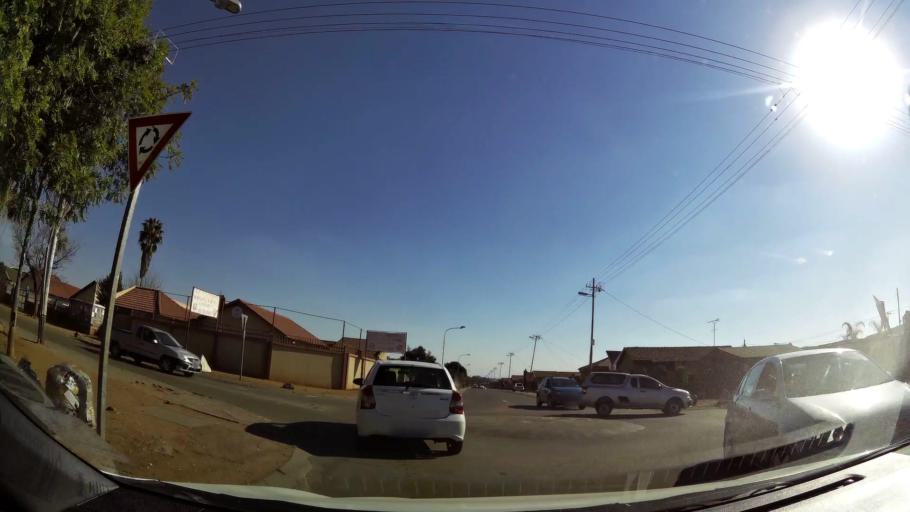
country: ZA
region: Gauteng
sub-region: City of Tshwane Metropolitan Municipality
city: Cullinan
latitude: -25.7120
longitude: 28.3898
